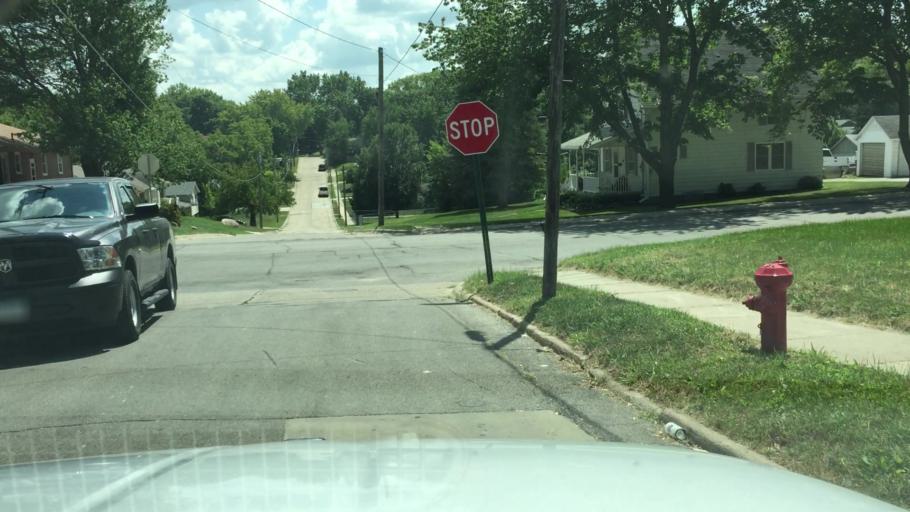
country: US
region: Iowa
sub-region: Jasper County
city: Newton
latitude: 41.6928
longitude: -93.0549
